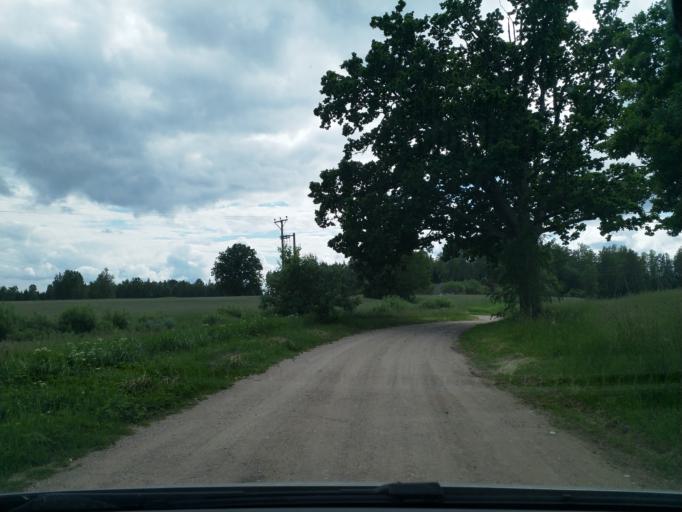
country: LV
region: Kuldigas Rajons
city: Kuldiga
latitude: 56.8356
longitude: 21.9555
